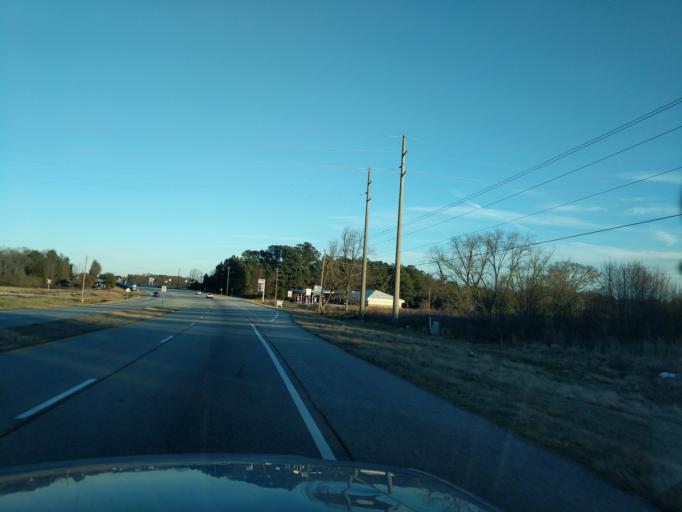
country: US
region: Georgia
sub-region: Franklin County
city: Lavonia
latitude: 34.4476
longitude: -83.1406
